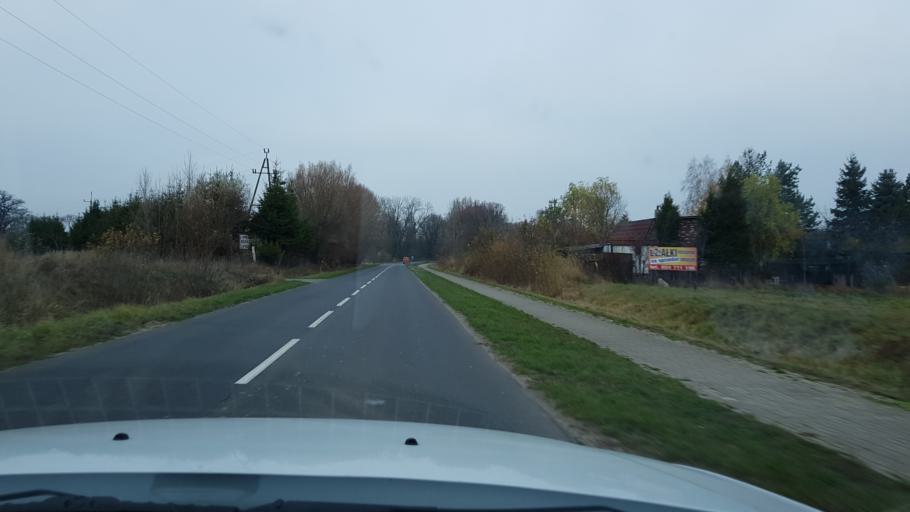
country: PL
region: West Pomeranian Voivodeship
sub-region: Powiat kamienski
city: Kamien Pomorski
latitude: 53.9884
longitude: 14.6889
